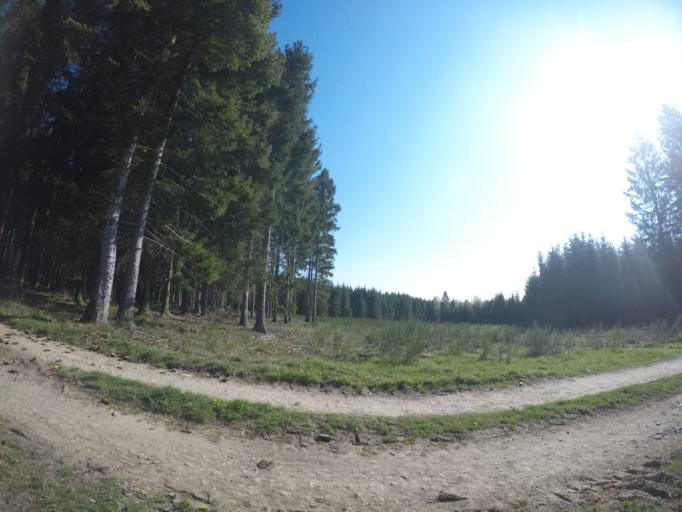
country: BE
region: Wallonia
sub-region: Province du Luxembourg
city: Leglise
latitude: 49.7991
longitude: 5.5860
